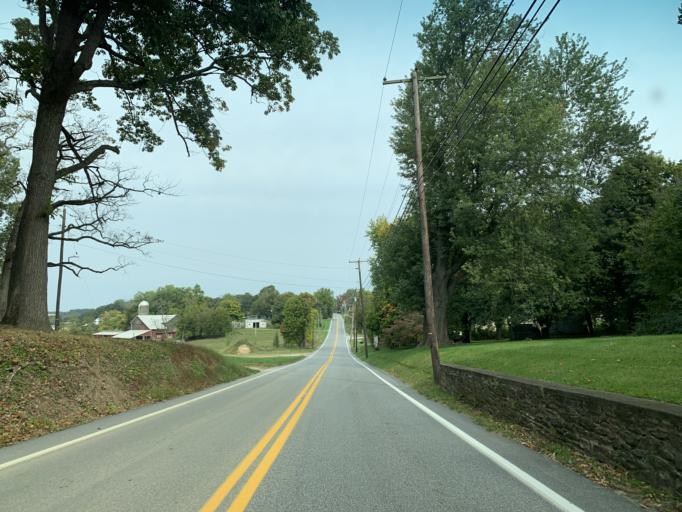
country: US
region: Pennsylvania
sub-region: York County
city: Susquehanna Trails
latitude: 39.7309
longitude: -76.4517
